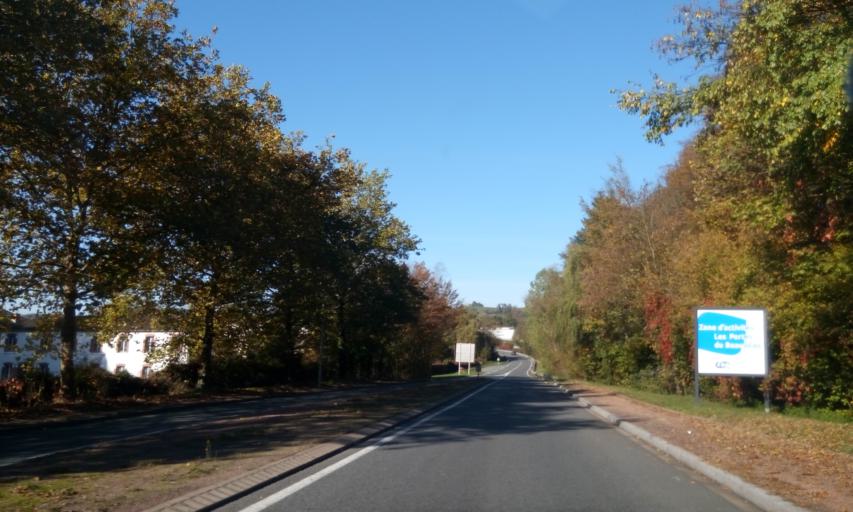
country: FR
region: Rhone-Alpes
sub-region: Departement du Rhone
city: Bourg-de-Thizy
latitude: 46.0322
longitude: 4.2953
